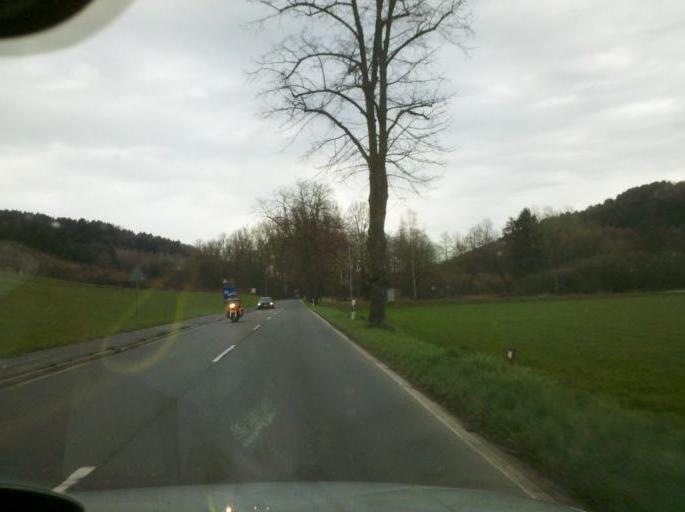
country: DE
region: North Rhine-Westphalia
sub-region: Regierungsbezirk Koln
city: Rosrath
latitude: 50.9344
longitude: 7.1947
